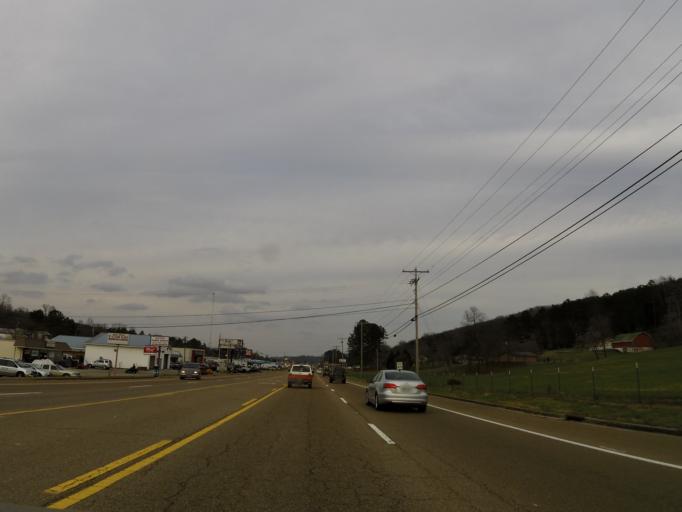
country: US
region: Tennessee
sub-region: Rhea County
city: Dayton
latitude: 35.4665
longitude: -85.0393
